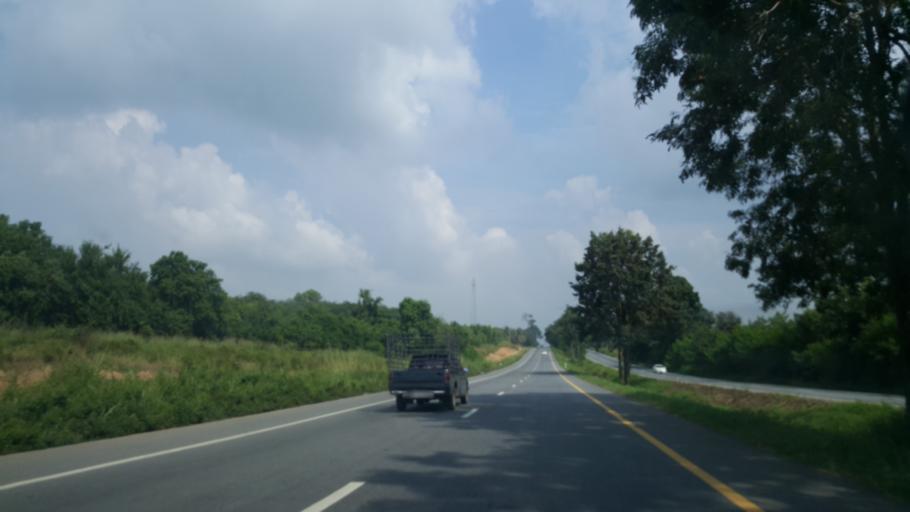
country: TH
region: Rayong
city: Ban Chang
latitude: 12.7788
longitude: 100.9918
